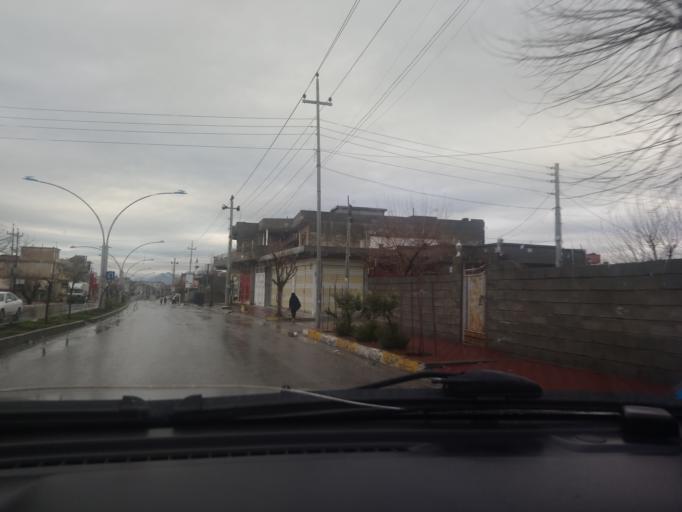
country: IQ
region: As Sulaymaniyah
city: Qeladize
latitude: 36.1792
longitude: 45.1362
